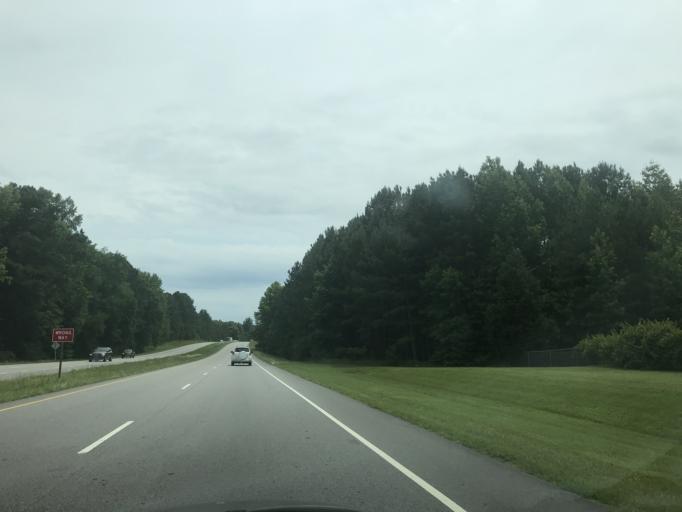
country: US
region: North Carolina
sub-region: Franklin County
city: Franklinton
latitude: 36.2069
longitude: -78.4485
